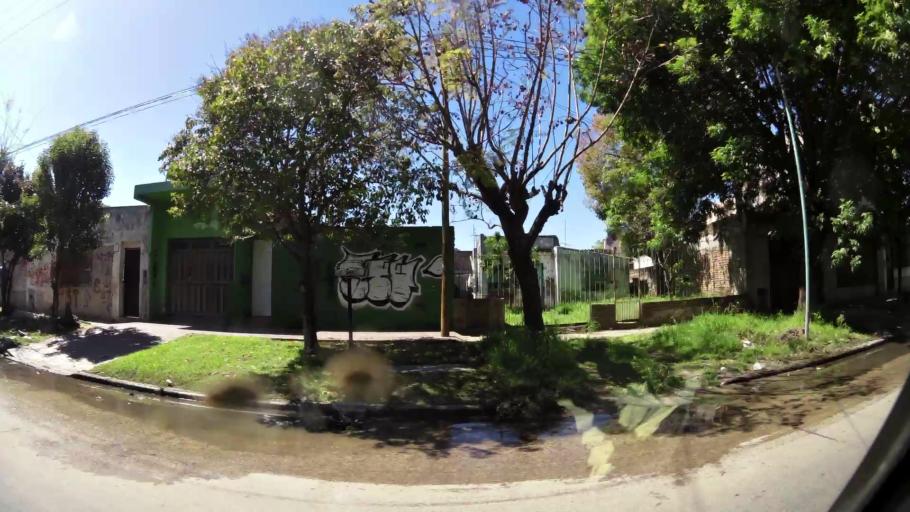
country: AR
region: Buenos Aires
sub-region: Partido de Quilmes
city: Quilmes
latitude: -34.7220
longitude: -58.3116
